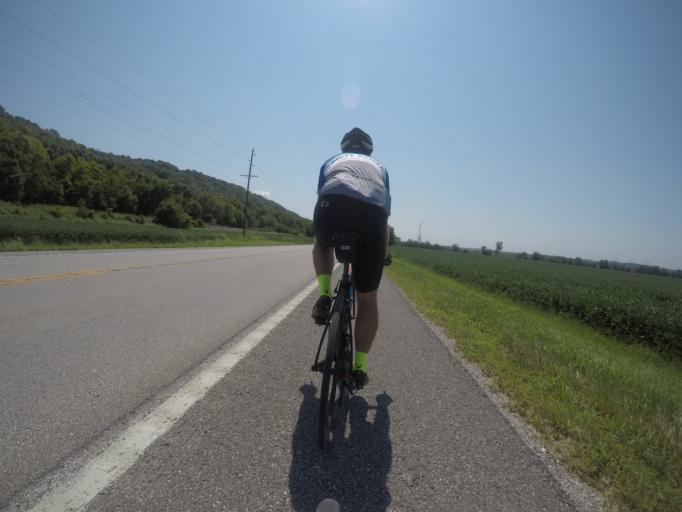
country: US
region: Missouri
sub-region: Platte County
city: Weston
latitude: 39.4916
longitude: -94.9986
